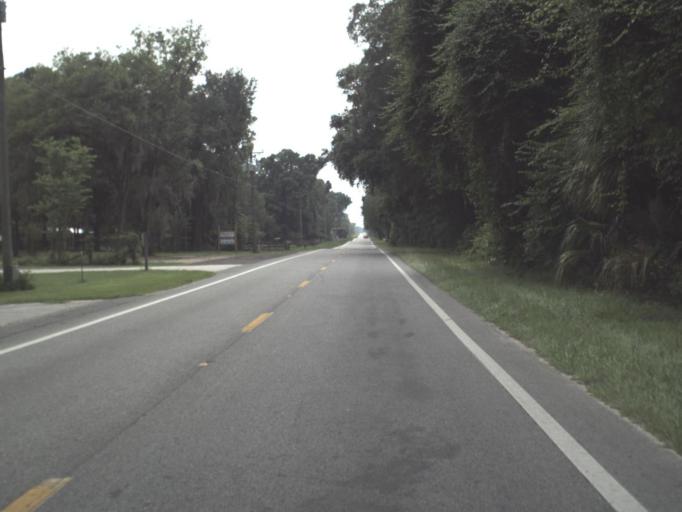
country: US
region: Florida
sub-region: Levy County
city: Chiefland
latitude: 29.4705
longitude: -82.8893
